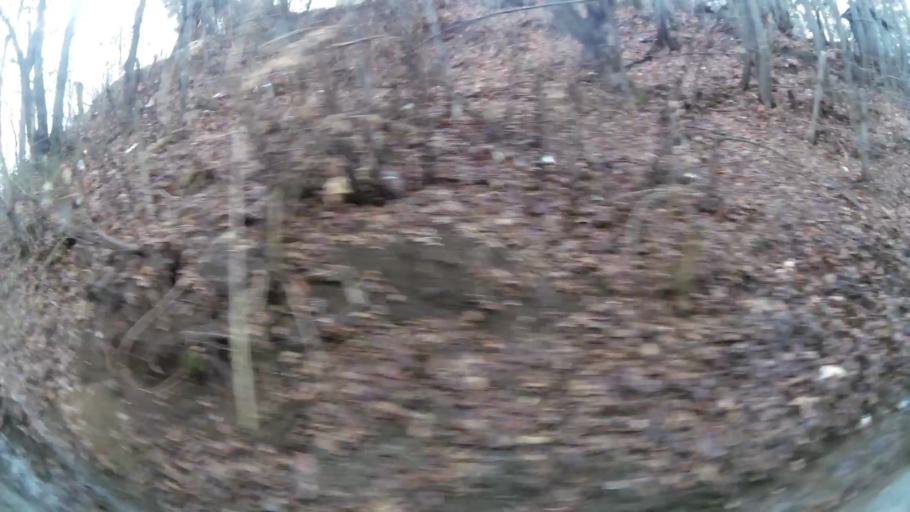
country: BG
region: Sofia-Capital
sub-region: Stolichna Obshtina
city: Sofia
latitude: 42.6023
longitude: 23.3877
